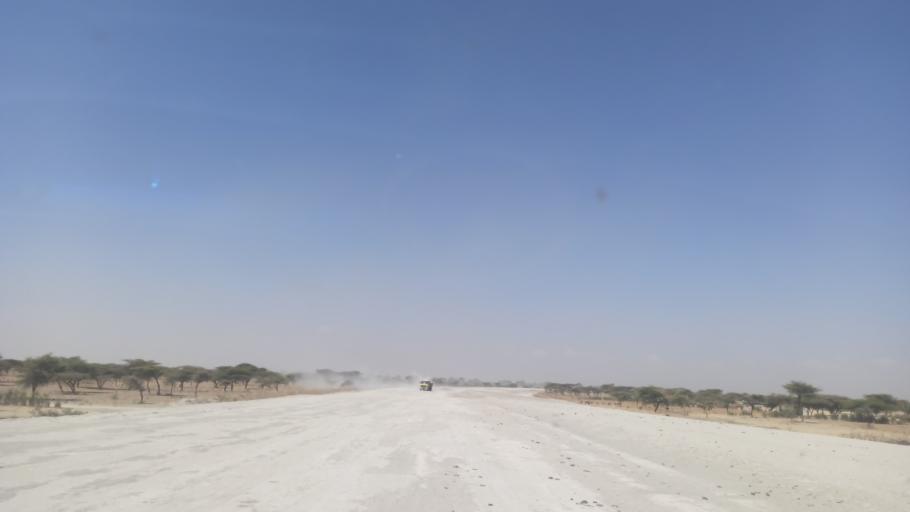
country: ET
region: Oromiya
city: Ziway
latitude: 7.6927
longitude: 38.6535
